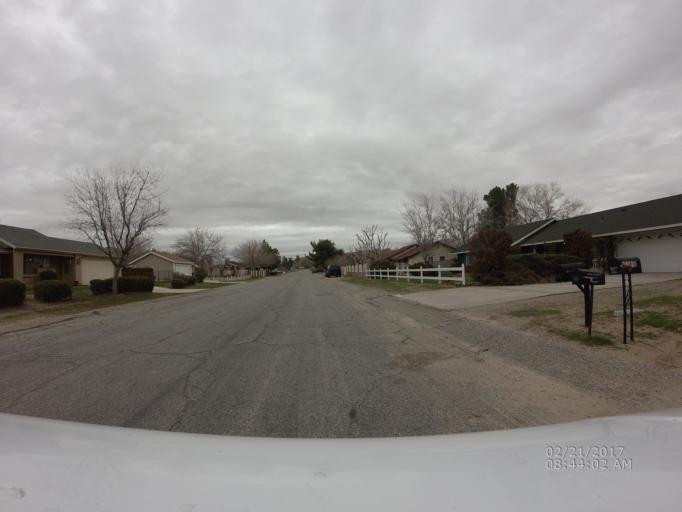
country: US
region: California
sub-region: Los Angeles County
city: Lake Los Angeles
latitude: 34.5958
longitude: -117.8312
